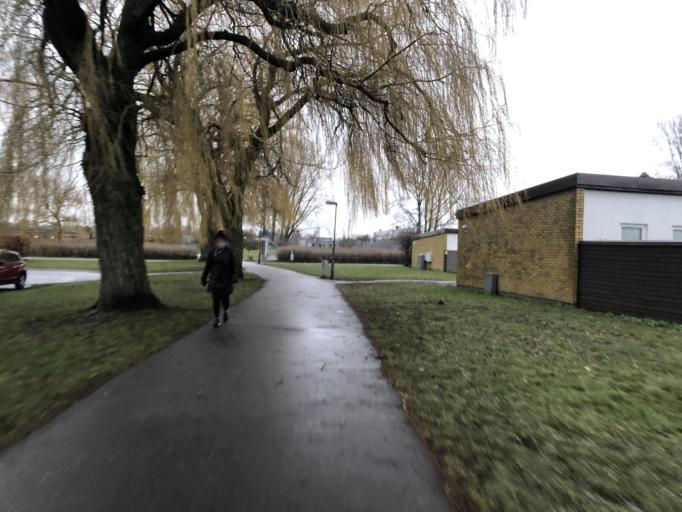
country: SE
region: Skane
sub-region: Burlovs Kommun
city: Arloev
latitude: 55.5882
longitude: 13.0670
